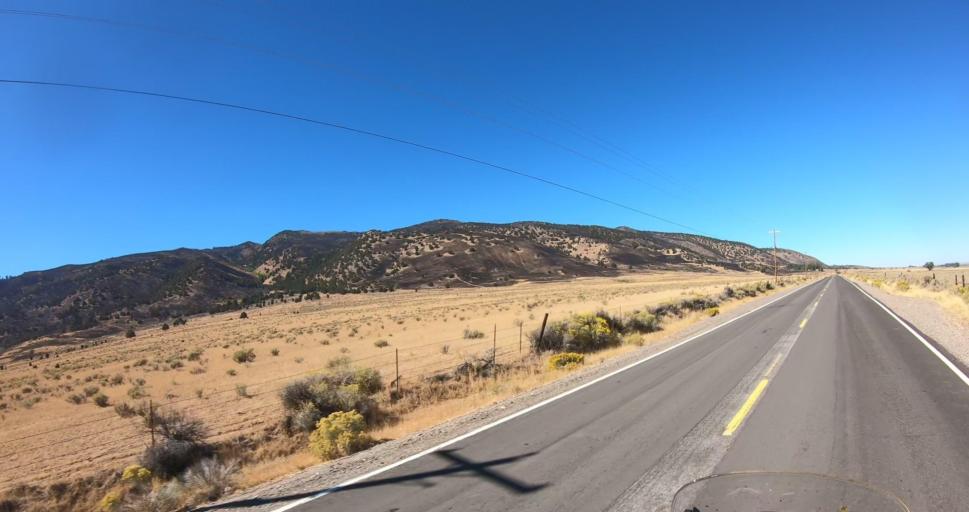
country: US
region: Oregon
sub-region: Lake County
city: Lakeview
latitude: 42.6263
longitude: -120.5108
